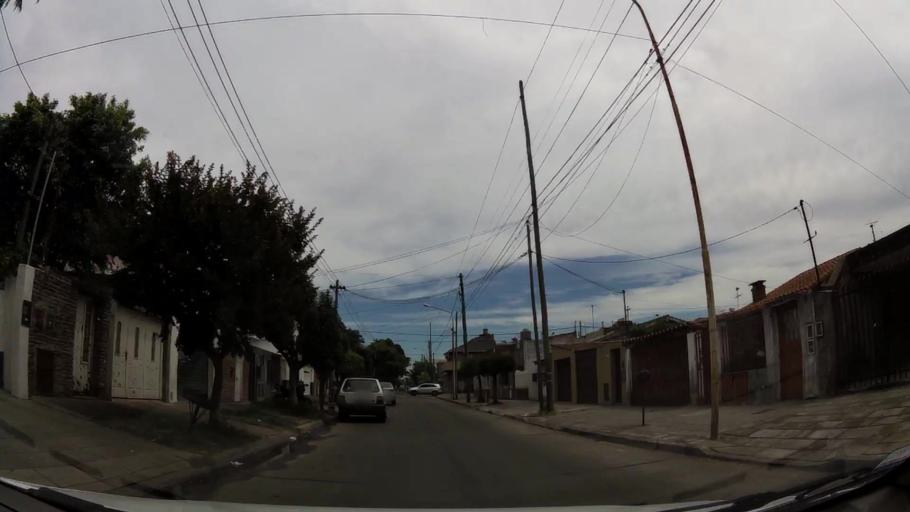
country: AR
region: Buenos Aires
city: San Justo
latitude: -34.6637
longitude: -58.5338
